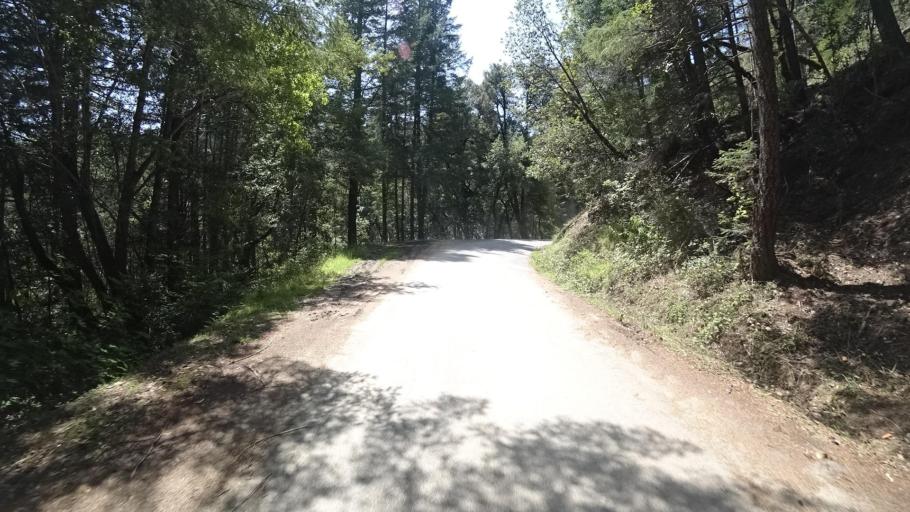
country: US
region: California
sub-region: Humboldt County
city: Redway
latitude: 40.1987
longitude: -123.5266
